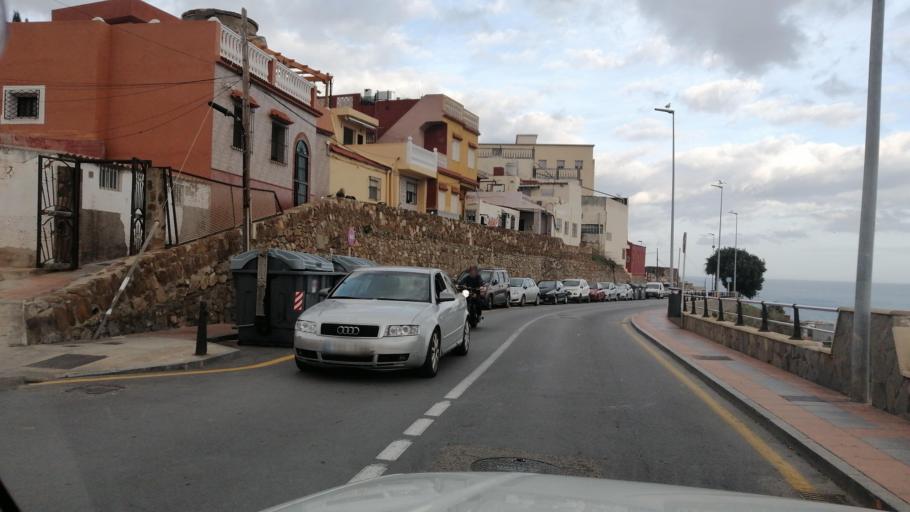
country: ES
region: Ceuta
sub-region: Ceuta
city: Ceuta
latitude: 35.8869
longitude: -5.3024
